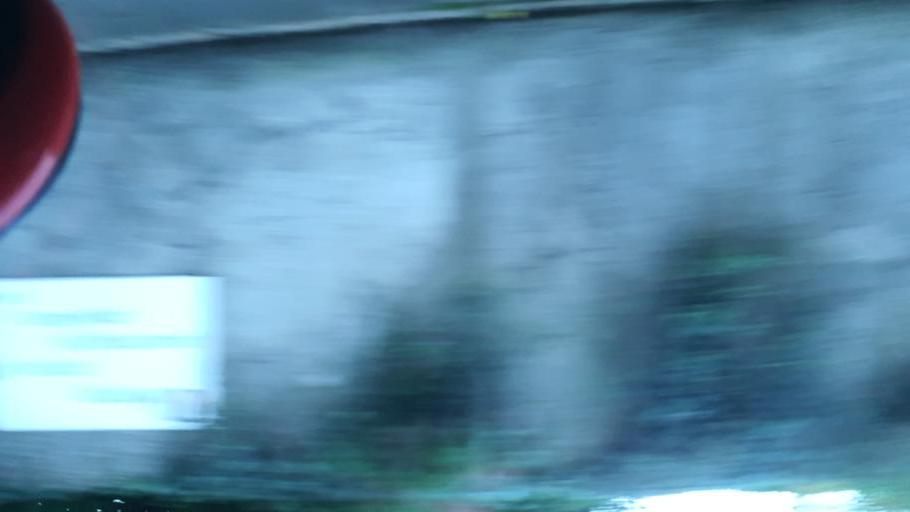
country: GB
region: Northern Ireland
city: Rostrevor
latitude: 54.1009
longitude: -6.1979
